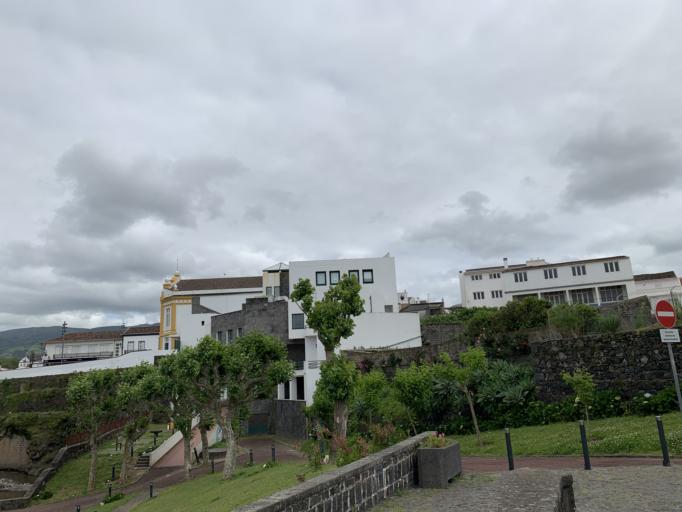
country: PT
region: Azores
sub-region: Ribeira Grande
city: Rabo de Peixe
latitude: 37.8226
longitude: -25.5213
